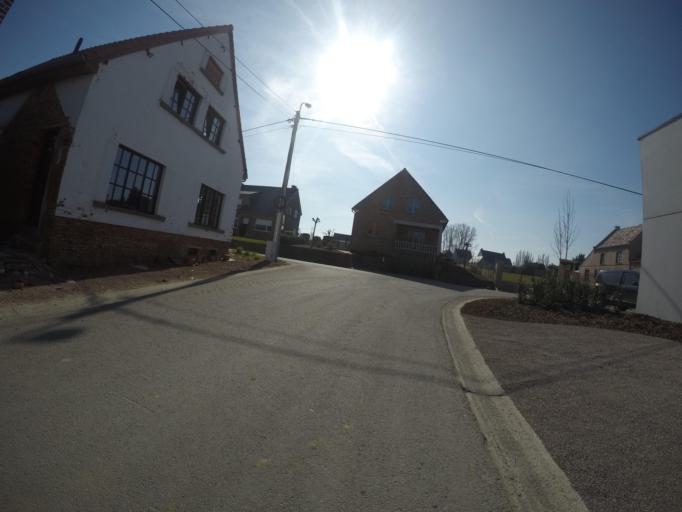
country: BE
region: Flanders
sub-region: Provincie Oost-Vlaanderen
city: Sint-Maria-Lierde
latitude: 50.8027
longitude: 3.8470
